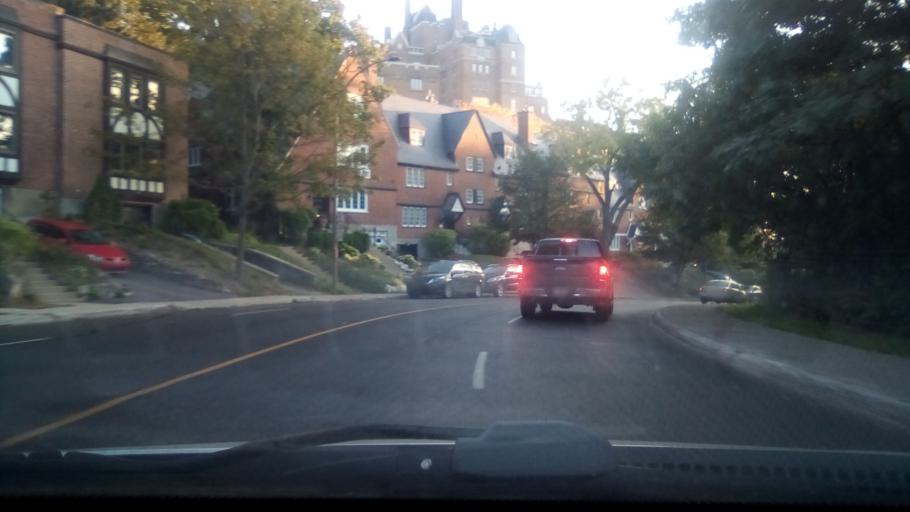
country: CA
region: Quebec
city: Westmount
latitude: 45.4939
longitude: -73.5955
